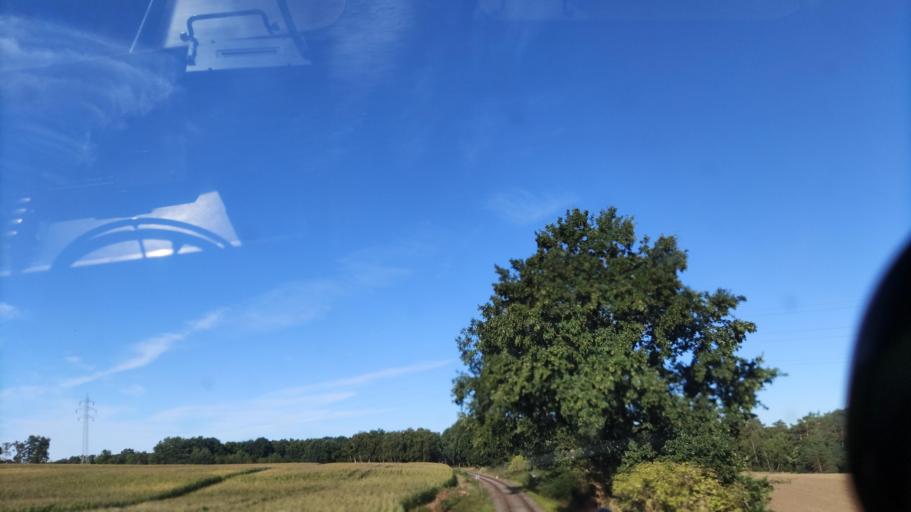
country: DE
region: Lower Saxony
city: Amelinghausen
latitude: 53.1397
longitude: 10.1824
